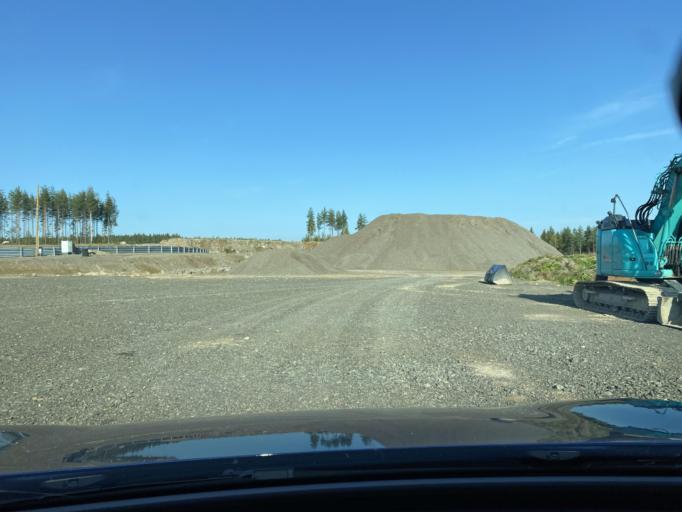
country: FI
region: Kymenlaakso
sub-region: Kouvola
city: Iitti
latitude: 60.8836
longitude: 26.4835
